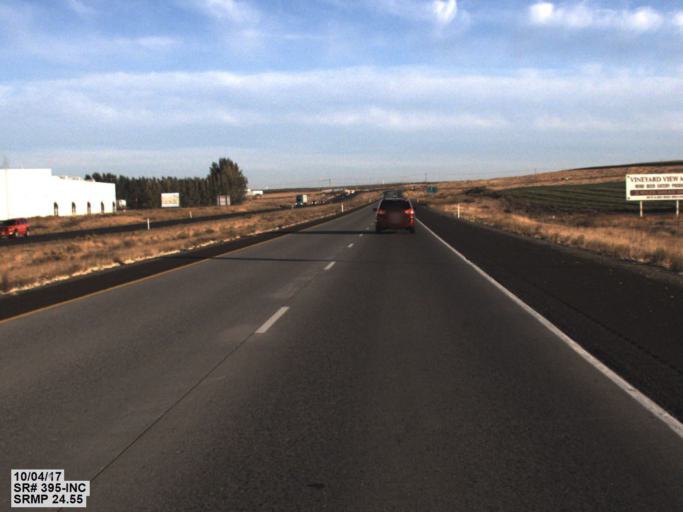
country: US
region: Washington
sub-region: Franklin County
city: Pasco
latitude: 46.2772
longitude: -119.0907
